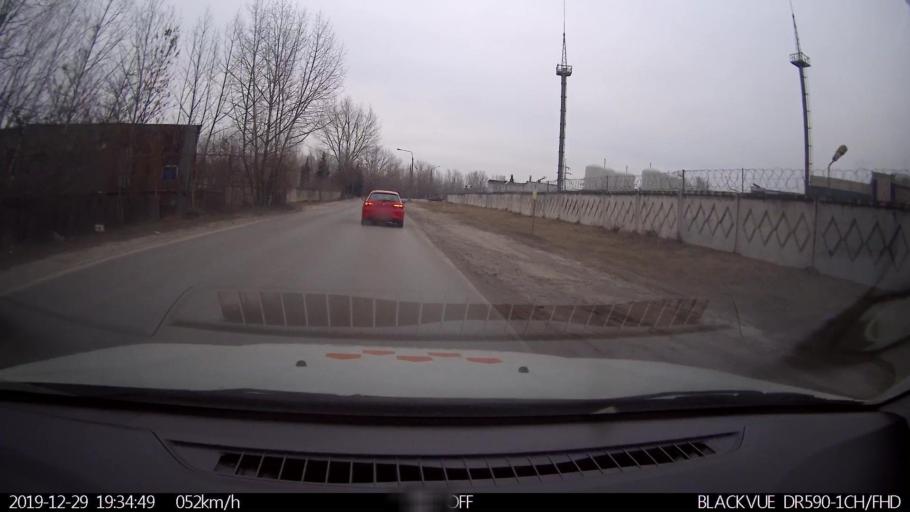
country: RU
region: Nizjnij Novgorod
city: Neklyudovo
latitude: 56.3552
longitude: 43.8939
